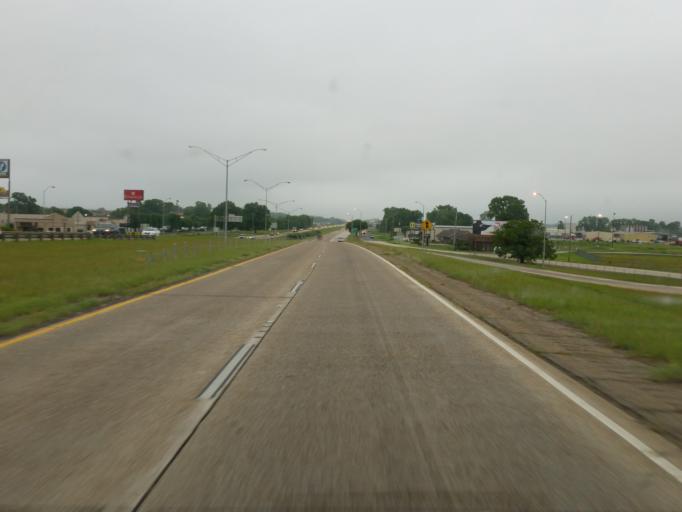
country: US
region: Louisiana
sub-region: Bossier Parish
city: Bossier City
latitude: 32.5286
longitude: -93.6734
